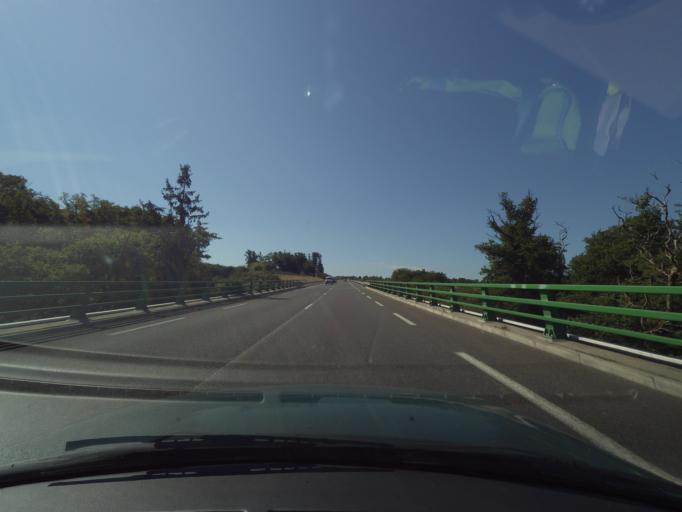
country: FR
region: Limousin
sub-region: Departement de la Haute-Vienne
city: Bellac
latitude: 46.1161
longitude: 1.0751
